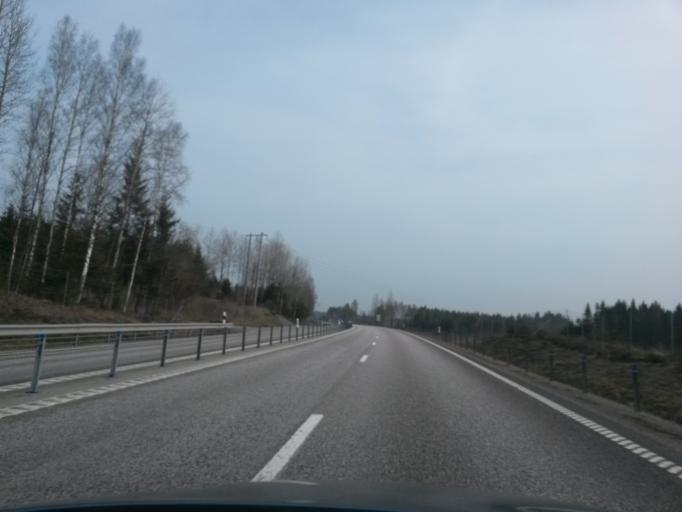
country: SE
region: Vaestra Goetaland
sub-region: Gullspangs Kommun
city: Anderstorp
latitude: 58.8967
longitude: 14.3296
